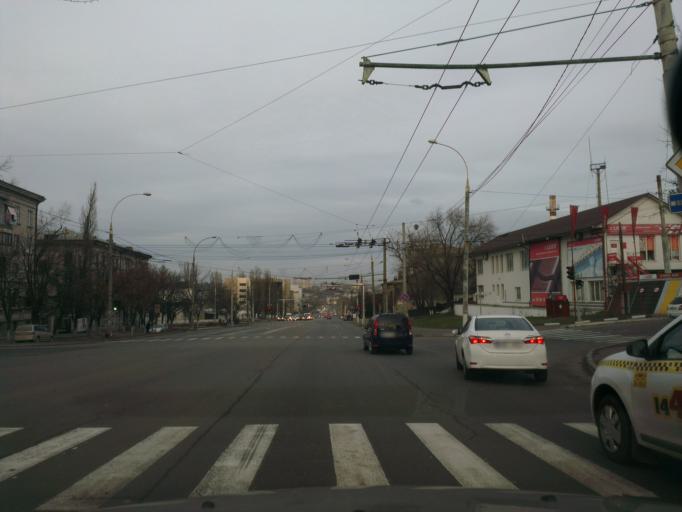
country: MD
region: Chisinau
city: Chisinau
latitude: 47.0350
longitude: 28.8205
